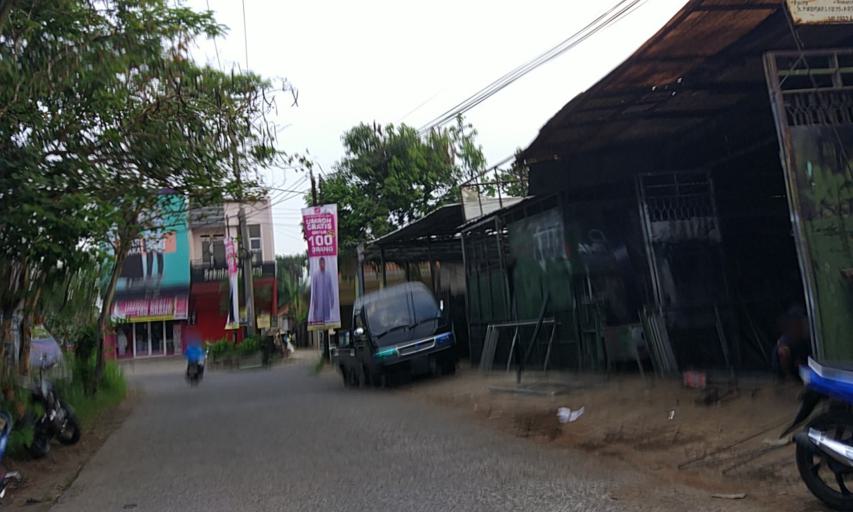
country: ID
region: West Java
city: Bandung
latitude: -6.9146
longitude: 107.6814
